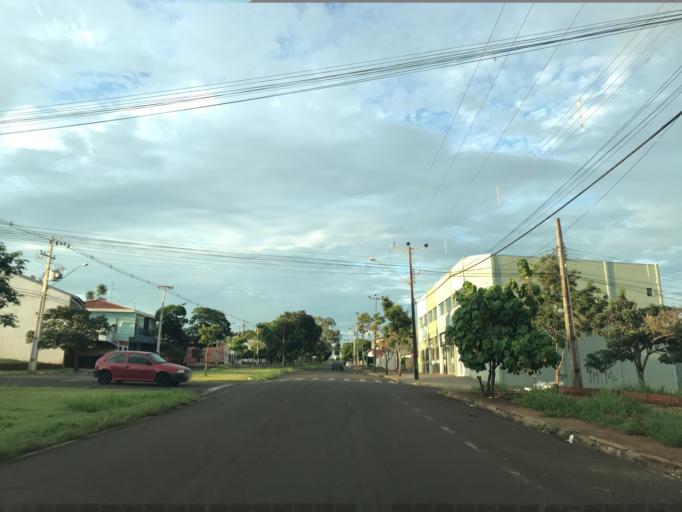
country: BR
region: Parana
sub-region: Maringa
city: Maringa
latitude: -23.3844
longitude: -51.9102
